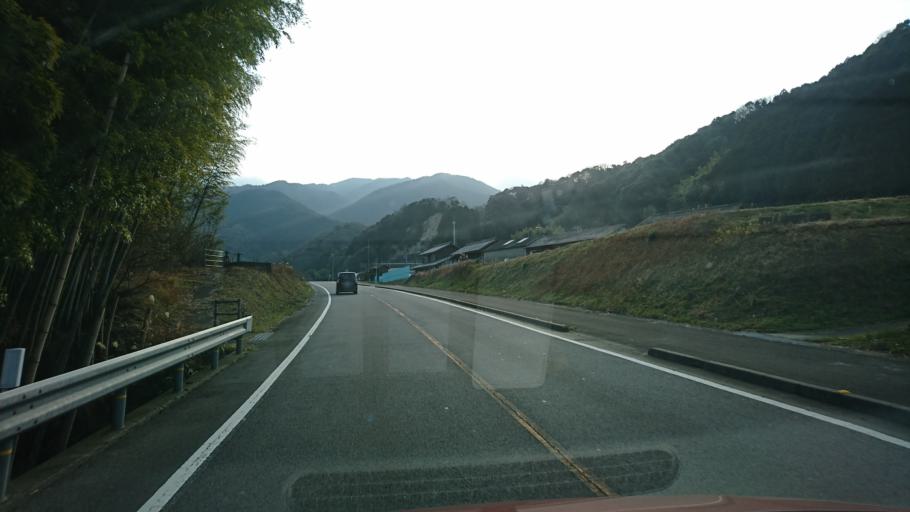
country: JP
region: Ehime
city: Hojo
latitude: 33.9771
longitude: 132.9044
